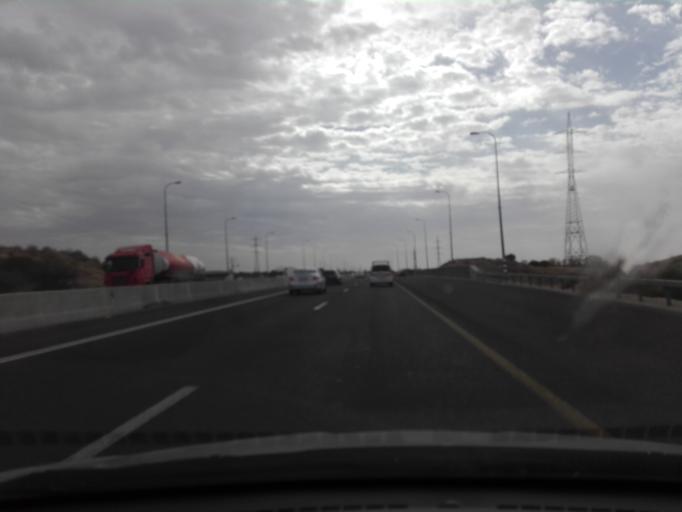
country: IL
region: Southern District
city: Lehavim
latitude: 31.3258
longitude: 34.7863
